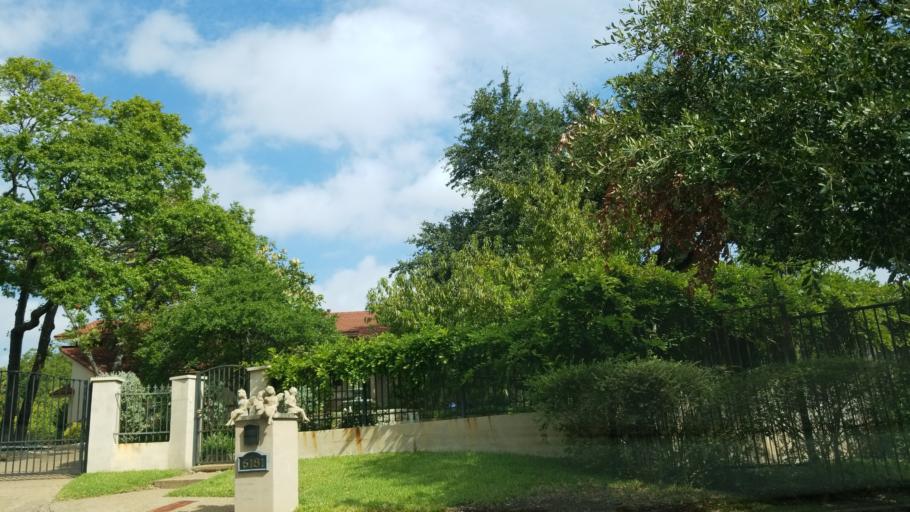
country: US
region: Texas
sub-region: Dallas County
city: Addison
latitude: 32.9360
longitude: -96.8018
